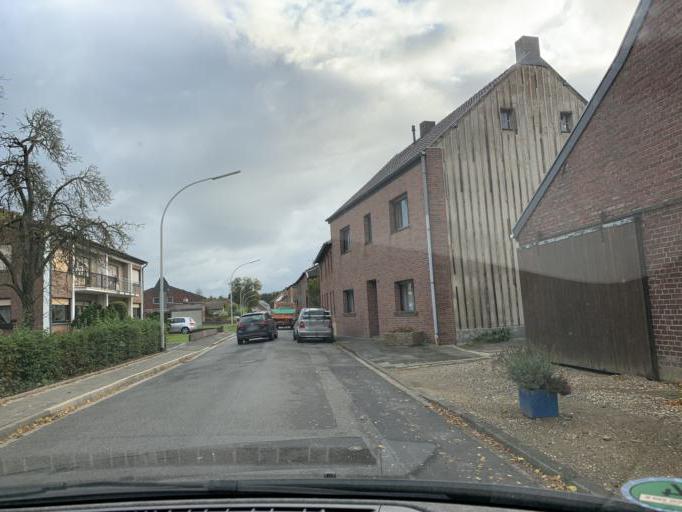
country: DE
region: North Rhine-Westphalia
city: Erkelenz
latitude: 51.1182
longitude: 6.3582
